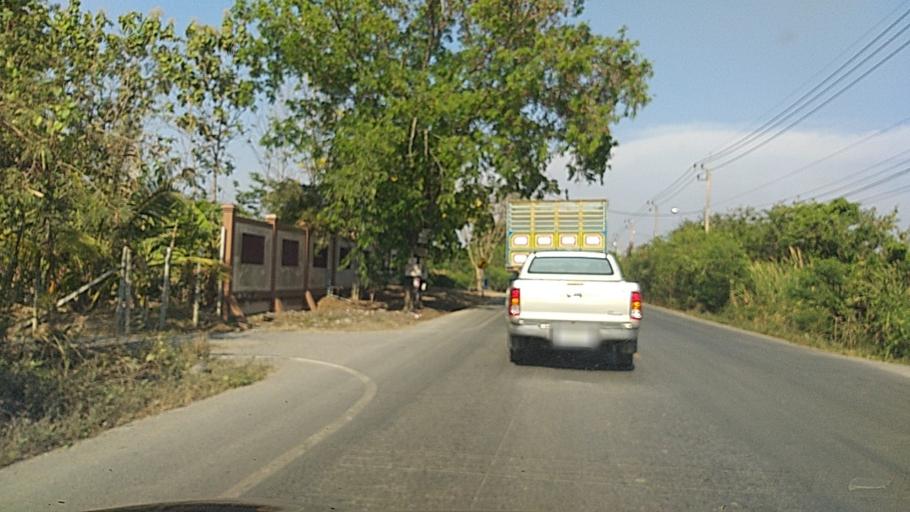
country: TH
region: Nonthaburi
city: Bang Yai
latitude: 13.8796
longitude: 100.3051
